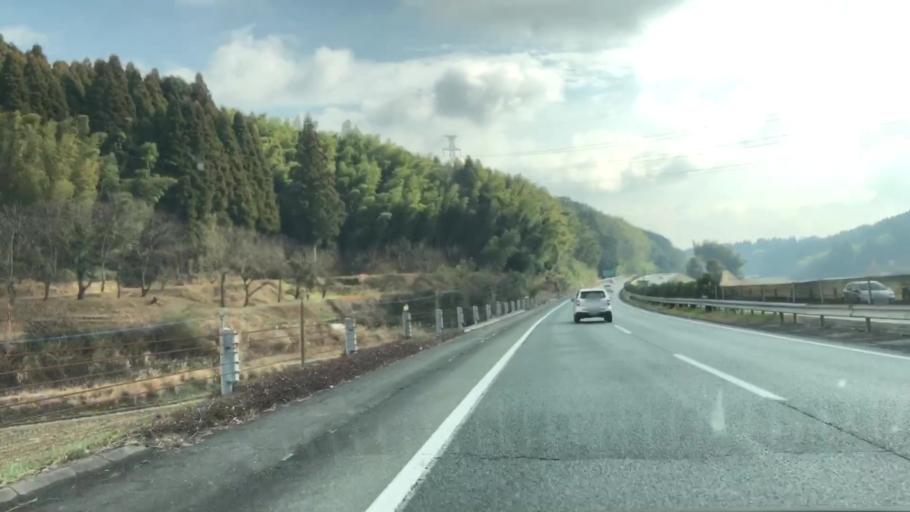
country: JP
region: Kumamoto
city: Yamaga
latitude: 33.0402
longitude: 130.5695
